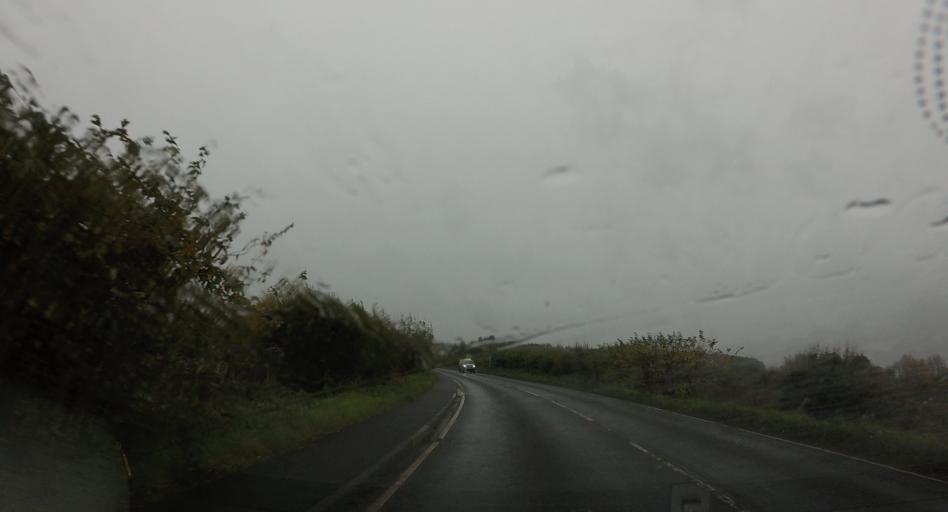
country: GB
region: Scotland
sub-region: Perth and Kinross
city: Coupar Angus
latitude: 56.5512
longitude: -3.2848
